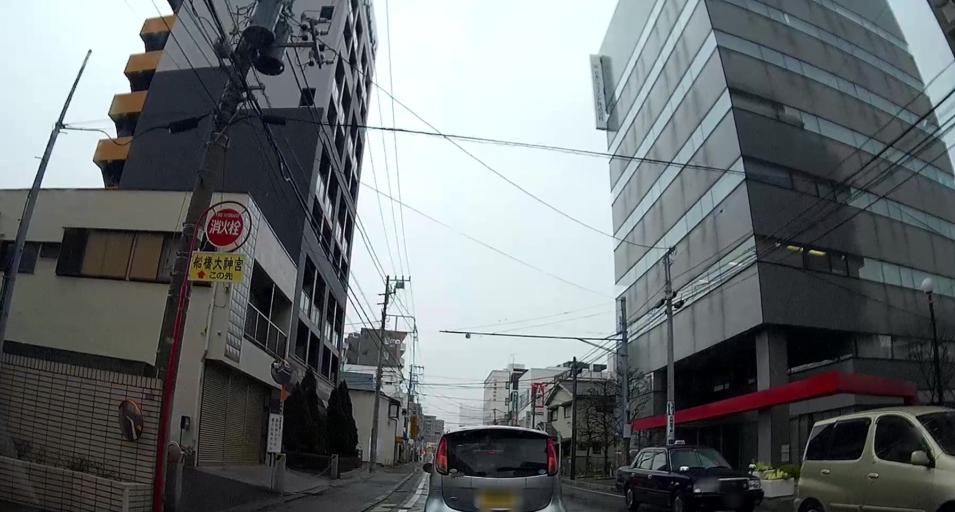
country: JP
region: Chiba
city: Funabashi
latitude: 35.6954
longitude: 139.9853
